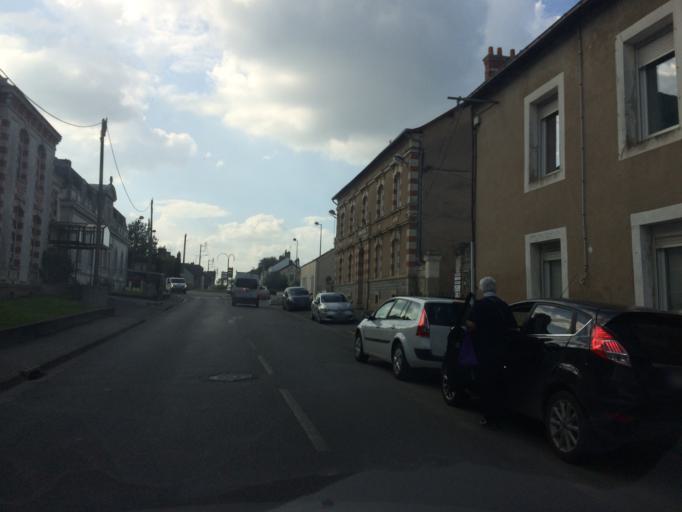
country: FR
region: Pays de la Loire
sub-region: Departement de la Loire-Atlantique
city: Blain
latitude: 47.4768
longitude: -1.7661
